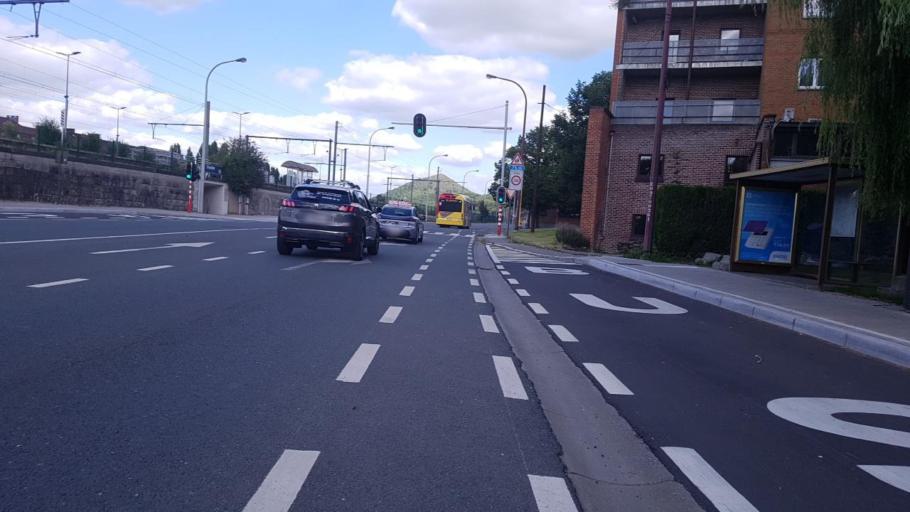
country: BE
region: Wallonia
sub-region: Province du Hainaut
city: Charleroi
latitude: 50.3924
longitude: 4.4679
